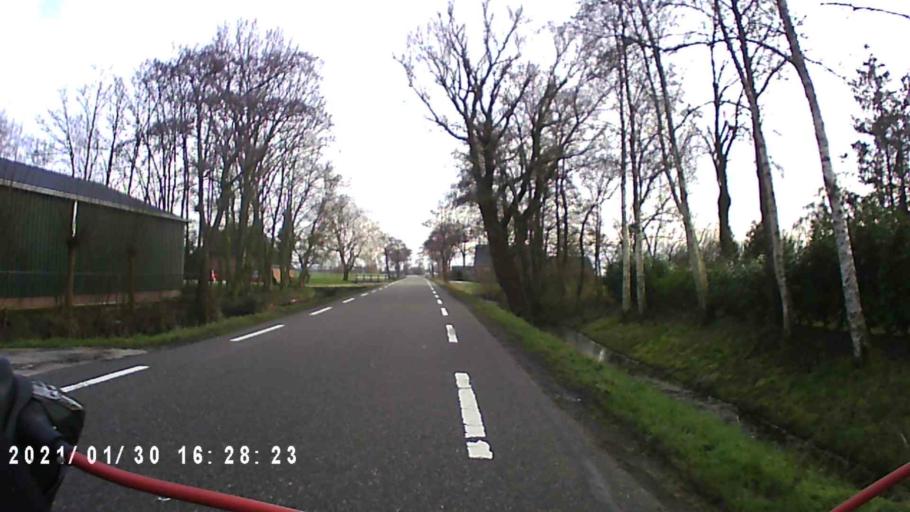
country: NL
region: Groningen
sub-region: Gemeente Zuidhorn
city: Zuidhorn
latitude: 53.2255
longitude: 6.3827
